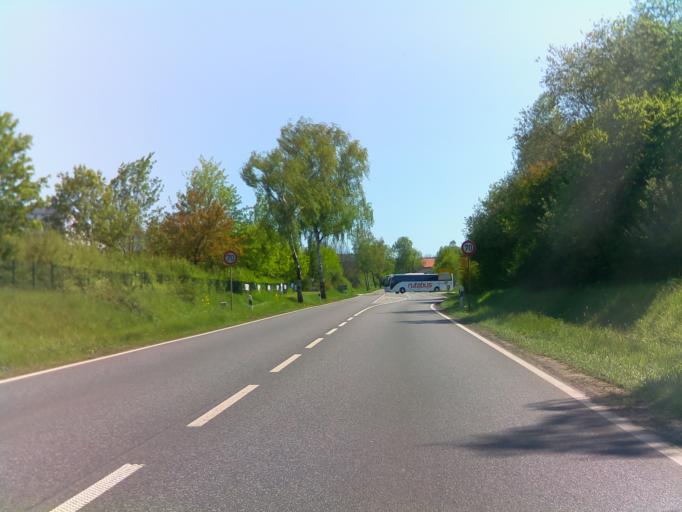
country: DE
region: Hesse
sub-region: Regierungsbezirk Giessen
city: Alsfeld
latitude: 50.7492
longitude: 9.2870
